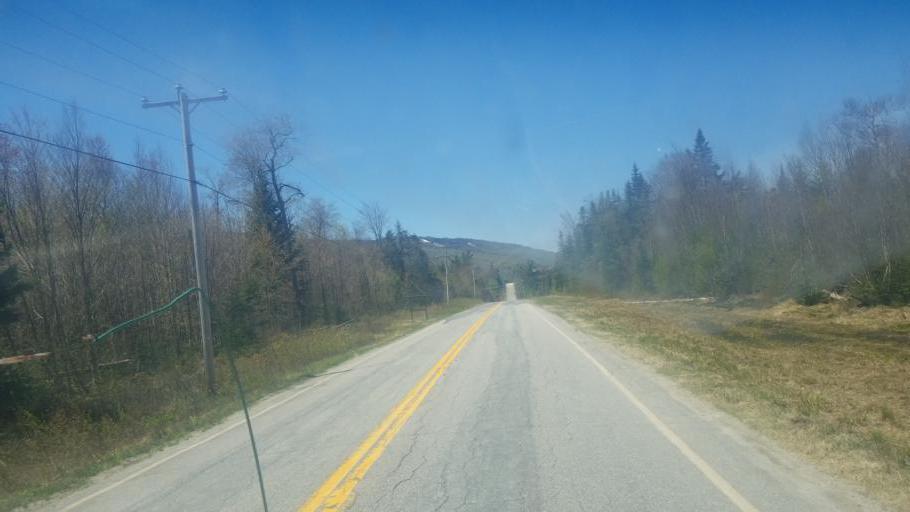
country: US
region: New Hampshire
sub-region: Coos County
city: Jefferson
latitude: 44.2610
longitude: -71.4323
